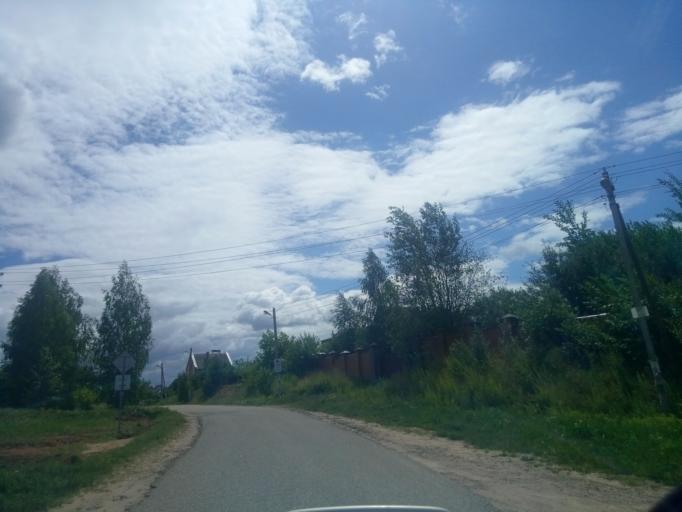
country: BY
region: Minsk
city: Zhdanovichy
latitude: 53.9388
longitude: 27.4089
